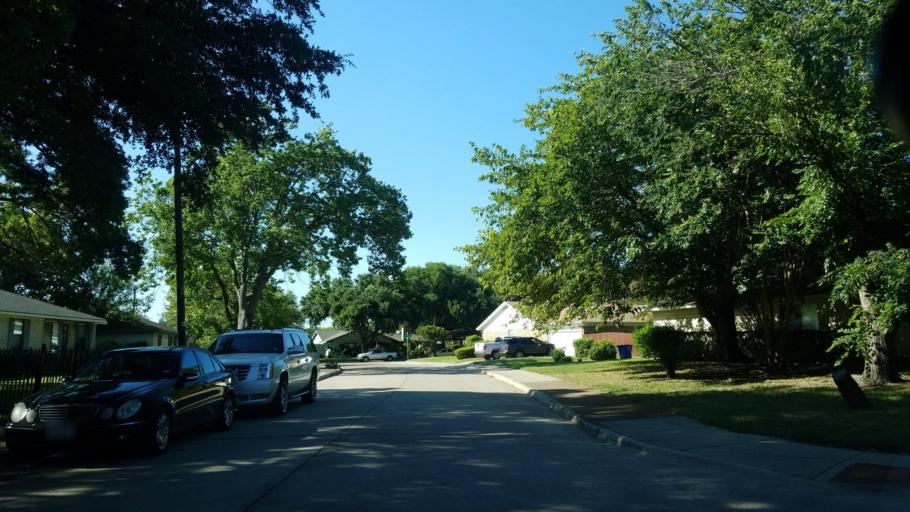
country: US
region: Texas
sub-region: Dallas County
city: Highland Park
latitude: 32.7895
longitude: -96.7103
